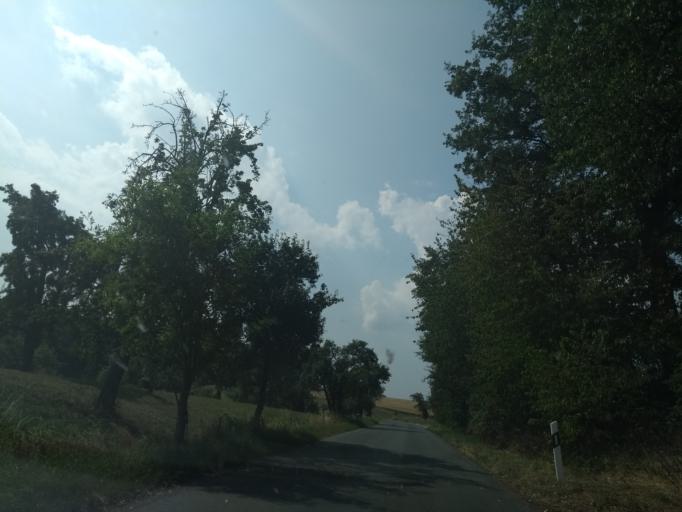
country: DE
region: Thuringia
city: Walpernhain
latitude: 51.0076
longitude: 11.9554
